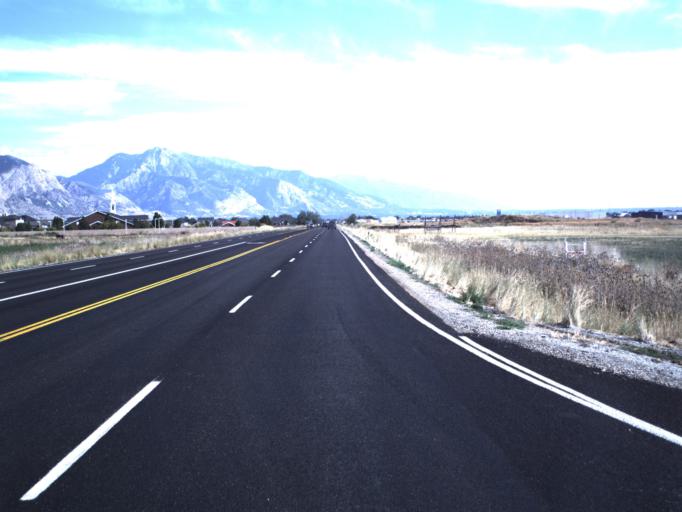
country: US
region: Utah
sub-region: Weber County
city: Pleasant View
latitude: 41.3244
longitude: -112.0191
